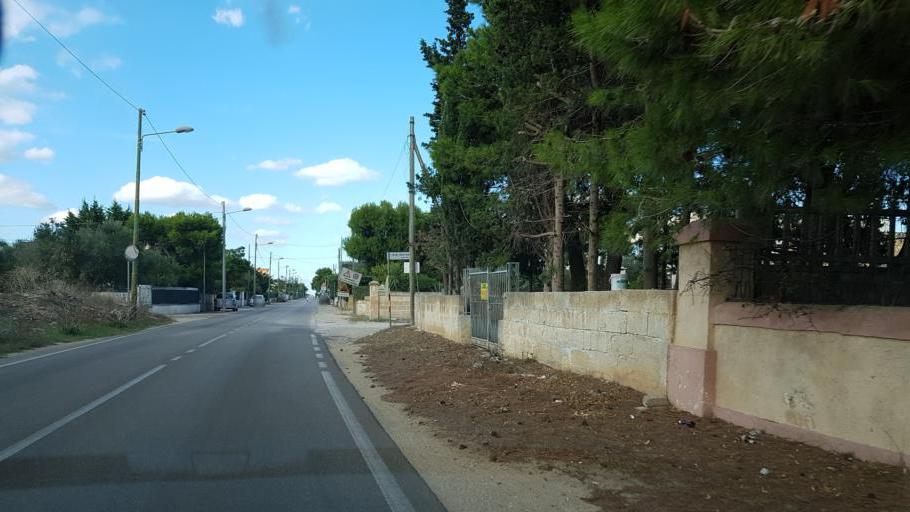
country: IT
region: Apulia
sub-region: Provincia di Lecce
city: Nardo
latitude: 40.1511
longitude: 18.0180
